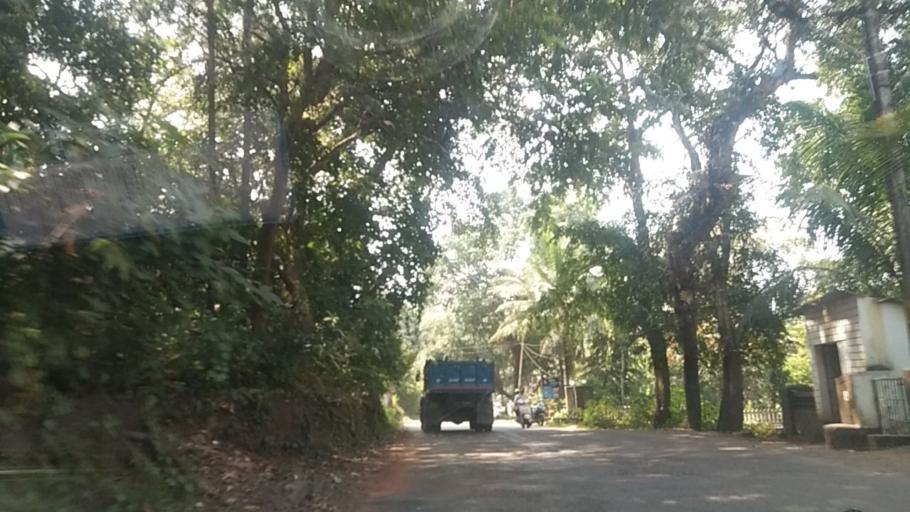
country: IN
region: Goa
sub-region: North Goa
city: Solim
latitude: 15.6149
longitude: 73.7804
